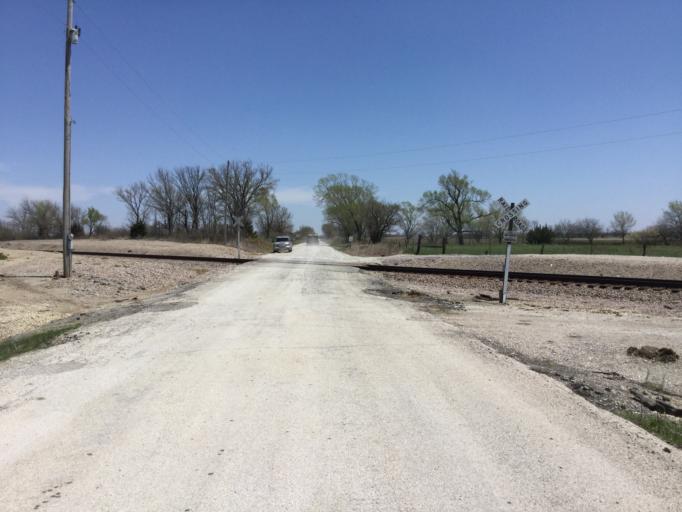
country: US
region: Kansas
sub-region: Bourbon County
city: Fort Scott
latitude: 37.7324
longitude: -94.7556
